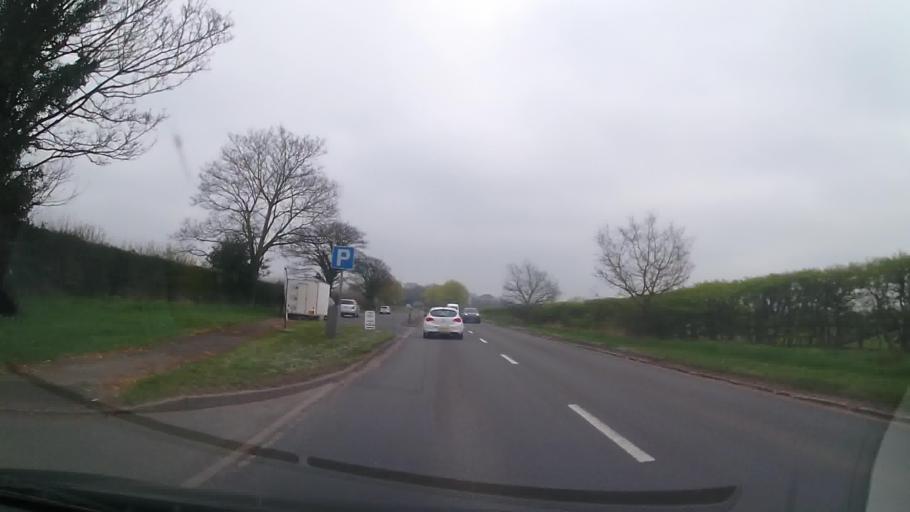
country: GB
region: England
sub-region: Shropshire
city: Market Drayton
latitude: 52.9132
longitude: -2.4531
